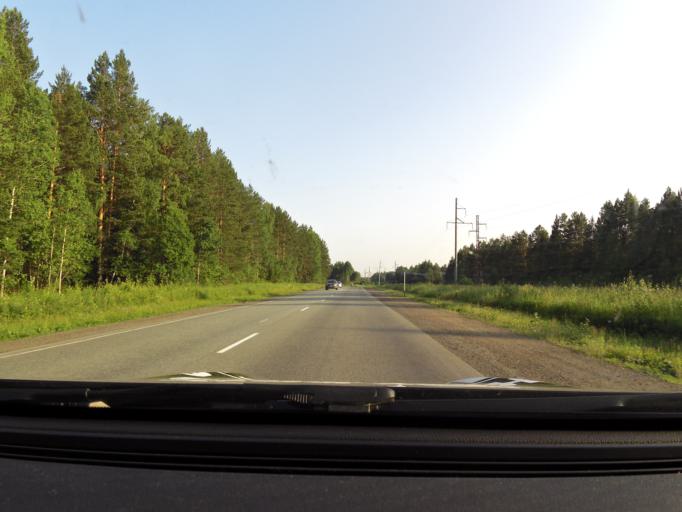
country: RU
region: Sverdlovsk
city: Nizhniye Sergi
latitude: 56.6129
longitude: 59.2296
